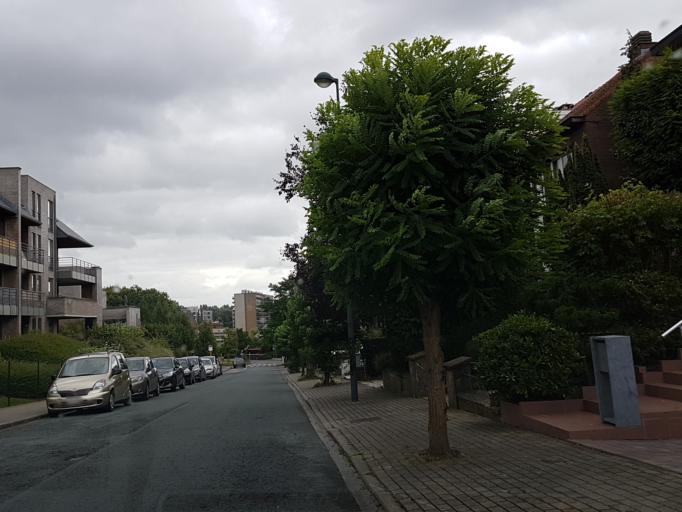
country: BE
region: Flanders
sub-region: Provincie Vlaams-Brabant
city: Kraainem
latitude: 50.8574
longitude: 4.4404
